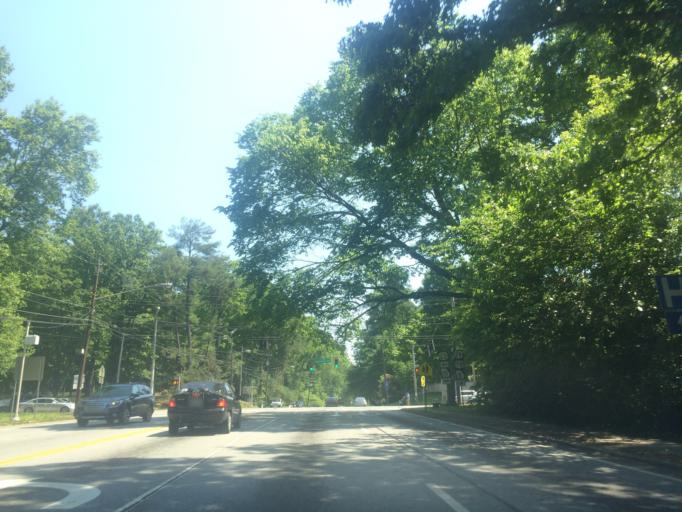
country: US
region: Georgia
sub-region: DeKalb County
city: North Decatur
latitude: 33.7844
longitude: -84.3045
